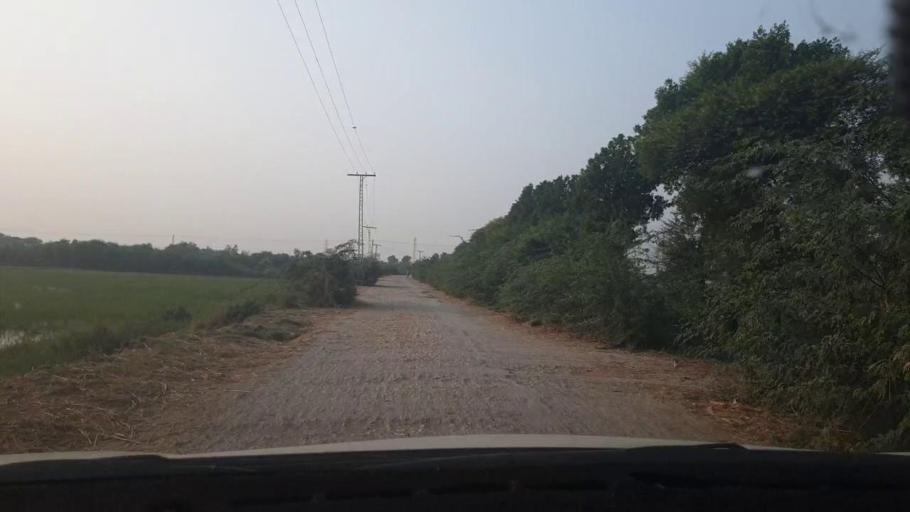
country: PK
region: Sindh
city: Bulri
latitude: 24.8563
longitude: 68.3367
